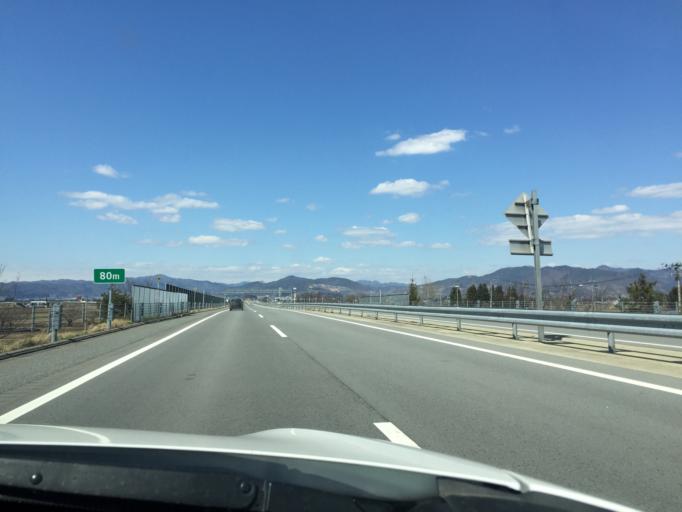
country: JP
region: Yamagata
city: Takahata
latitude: 37.9970
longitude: 140.1562
